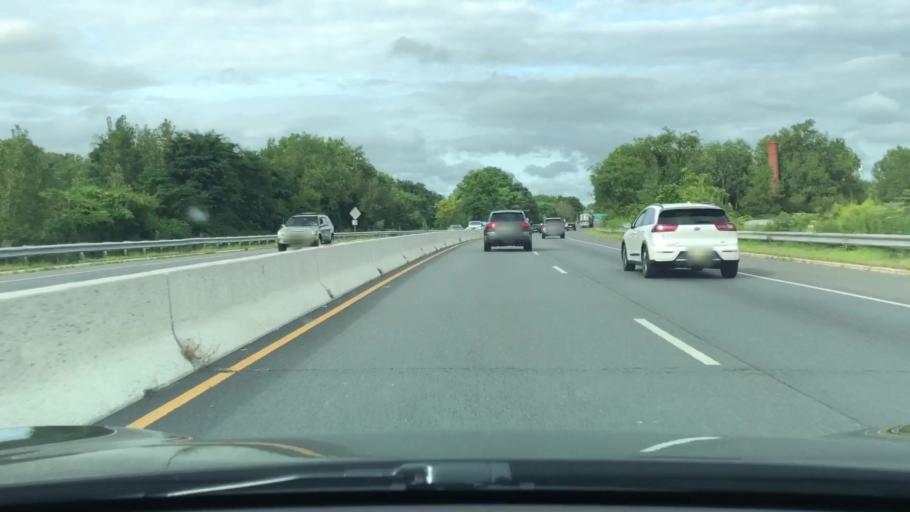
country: US
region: New Jersey
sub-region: Mercer County
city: Trenton
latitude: 40.2447
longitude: -74.7338
